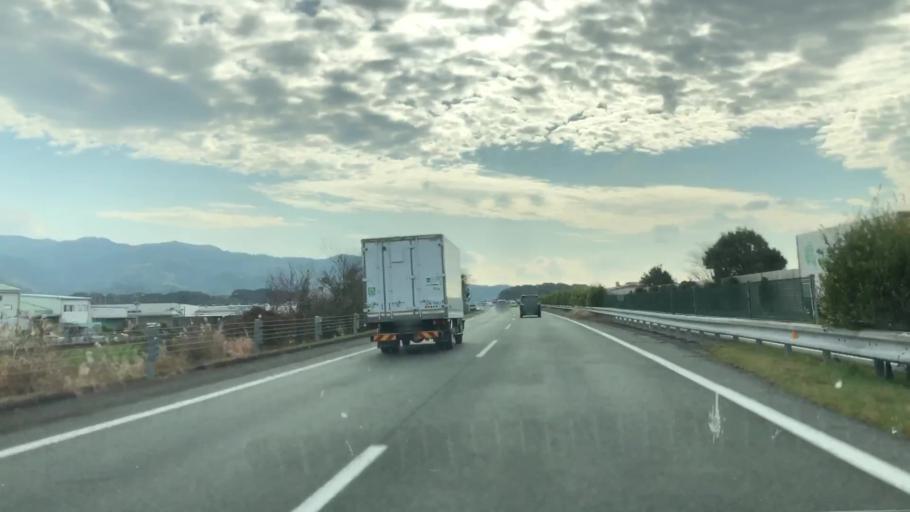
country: JP
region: Fukuoka
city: Setakamachi-takayanagi
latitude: 33.1885
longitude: 130.5197
